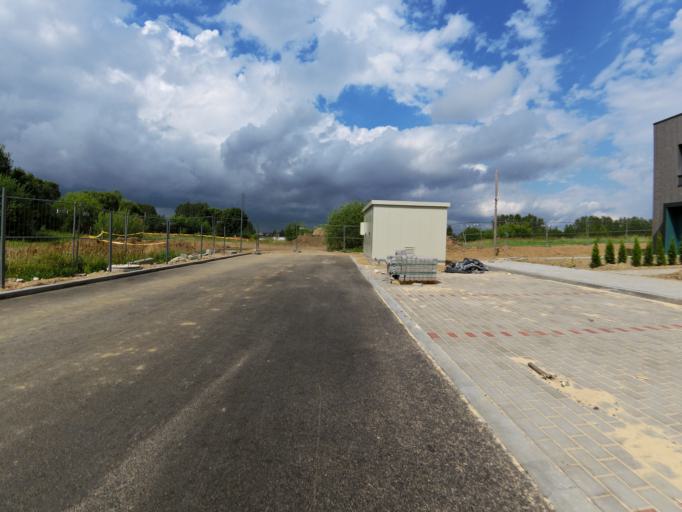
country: LT
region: Vilnius County
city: Pilaite
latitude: 54.7084
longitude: 25.1680
